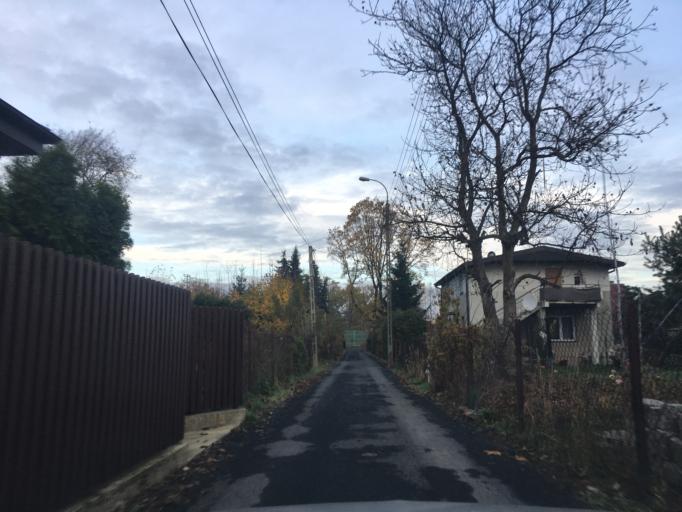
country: PL
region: Masovian Voivodeship
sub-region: Powiat pruszkowski
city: Brwinow
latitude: 52.1424
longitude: 20.7251
